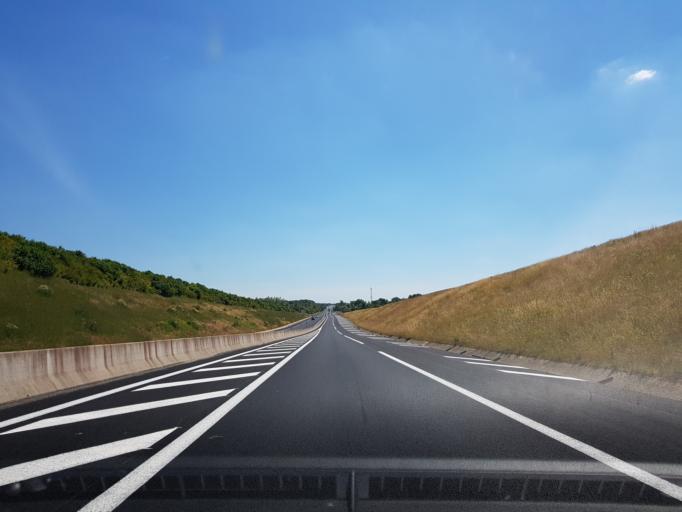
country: FR
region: Picardie
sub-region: Departement de la Somme
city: Nesle
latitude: 49.8349
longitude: 2.9155
